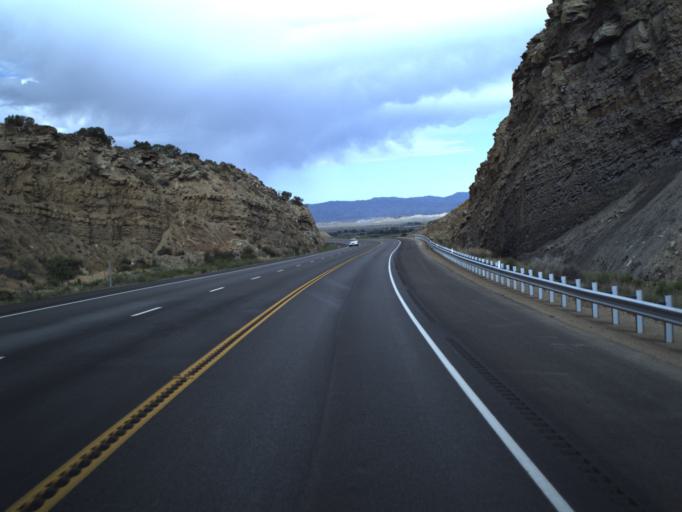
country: US
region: Utah
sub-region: Carbon County
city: Wellington
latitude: 39.5478
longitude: -110.6486
